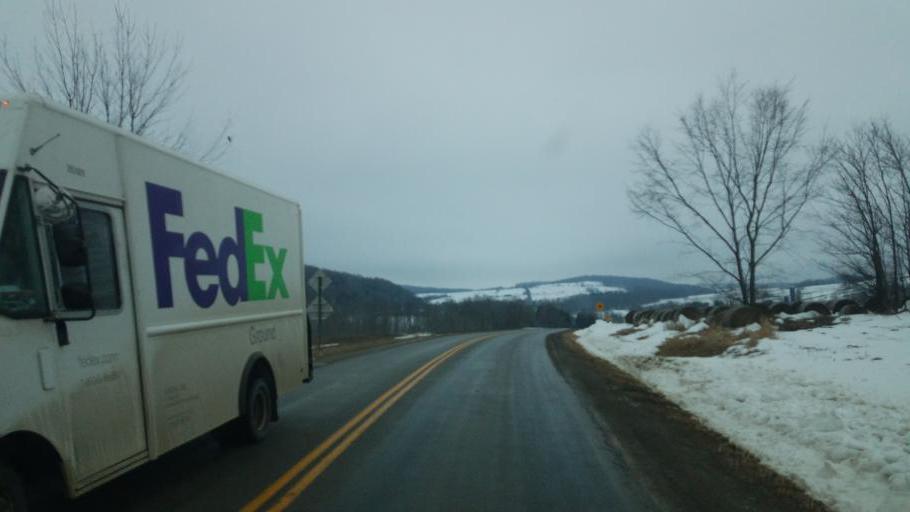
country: US
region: Pennsylvania
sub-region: Tioga County
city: Westfield
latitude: 42.0807
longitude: -77.4828
